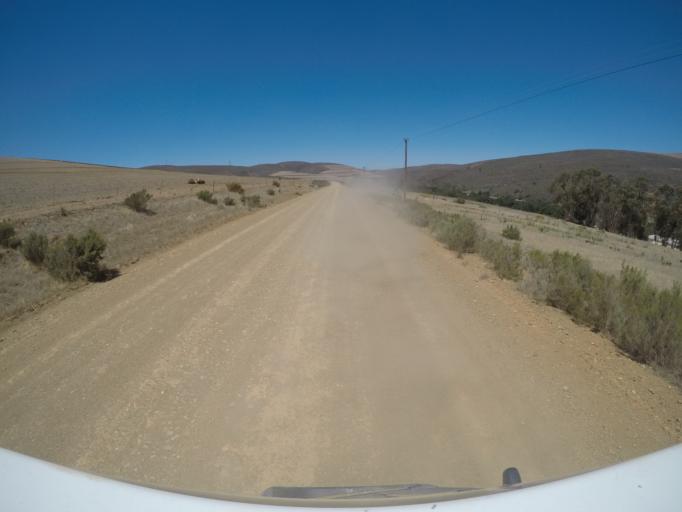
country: ZA
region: Western Cape
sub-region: Overberg District Municipality
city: Caledon
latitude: -34.1323
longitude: 19.2419
